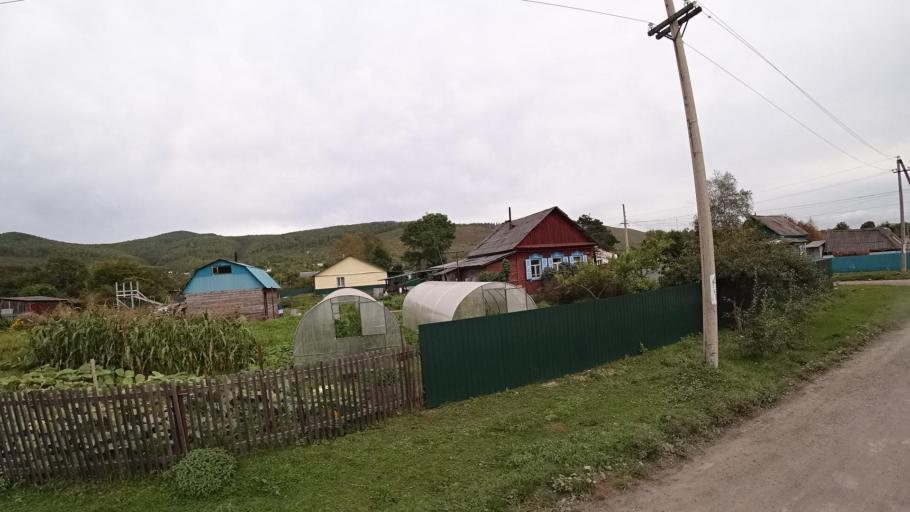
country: RU
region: Jewish Autonomous Oblast
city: Khingansk
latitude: 49.0356
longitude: 131.0495
